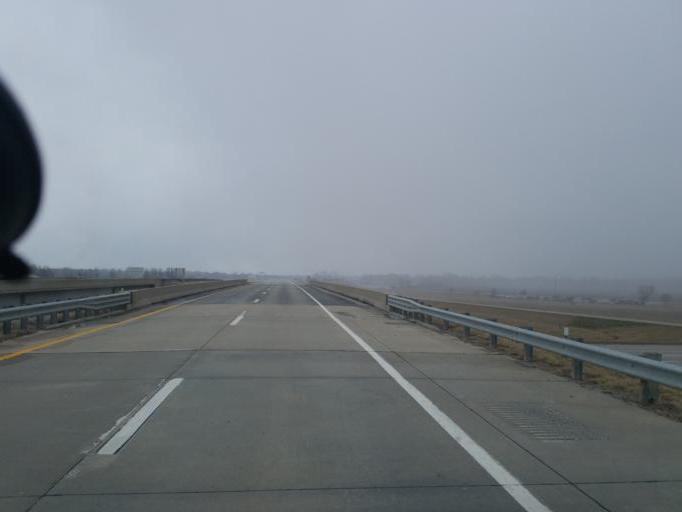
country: US
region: Missouri
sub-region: Randolph County
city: Moberly
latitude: 39.4446
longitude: -92.4250
